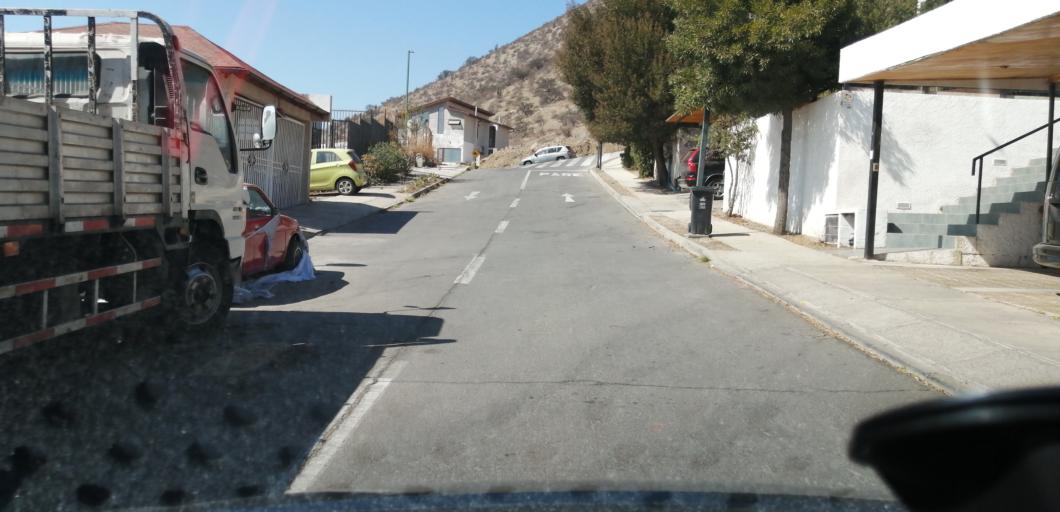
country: CL
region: Santiago Metropolitan
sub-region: Provincia de Santiago
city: Lo Prado
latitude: -33.4589
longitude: -70.8243
